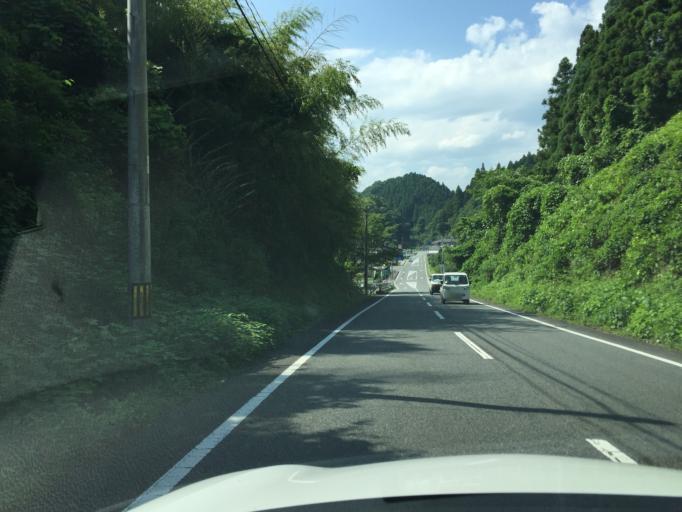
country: JP
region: Ibaraki
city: Kitaibaraki
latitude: 36.9509
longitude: 140.7066
